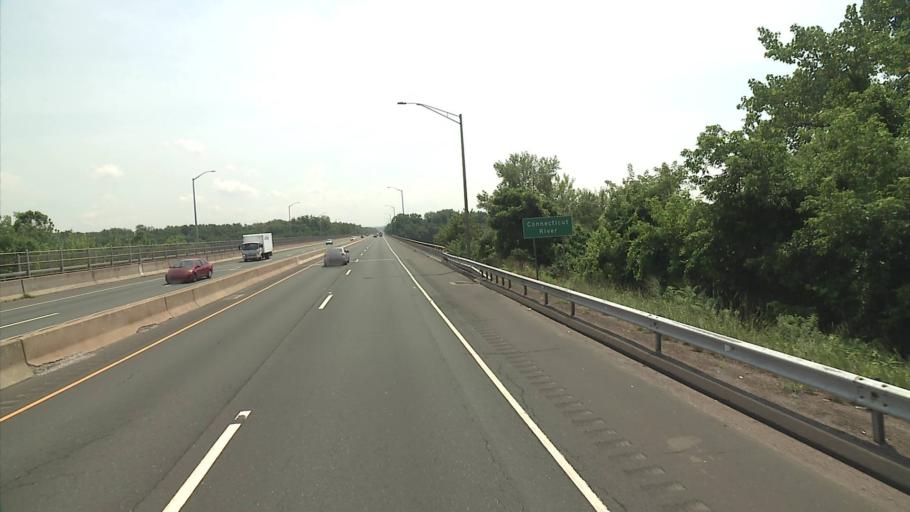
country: US
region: Connecticut
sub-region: Hartford County
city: South Windsor
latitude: 41.8139
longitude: -72.6476
